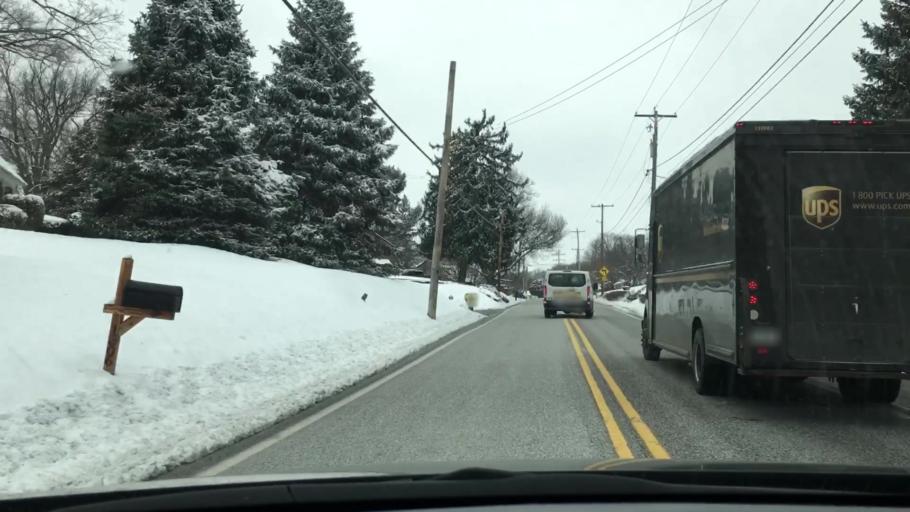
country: US
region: Pennsylvania
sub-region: York County
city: East York
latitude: 39.9880
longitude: -76.7062
